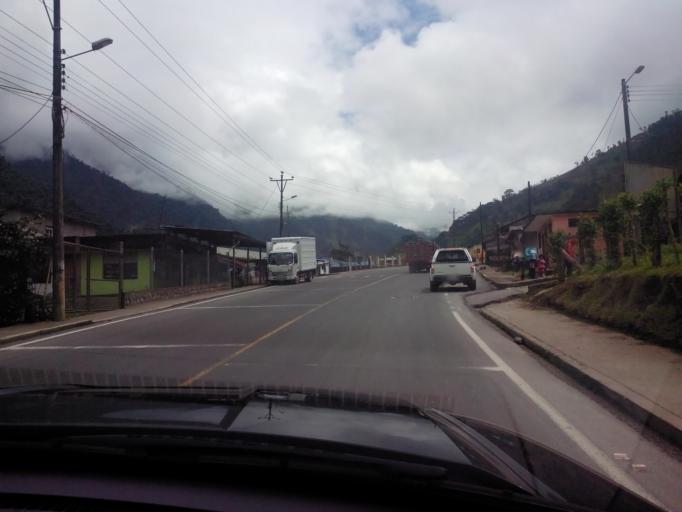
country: EC
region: Pichincha
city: Sangolqui
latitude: -0.4141
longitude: -78.0263
